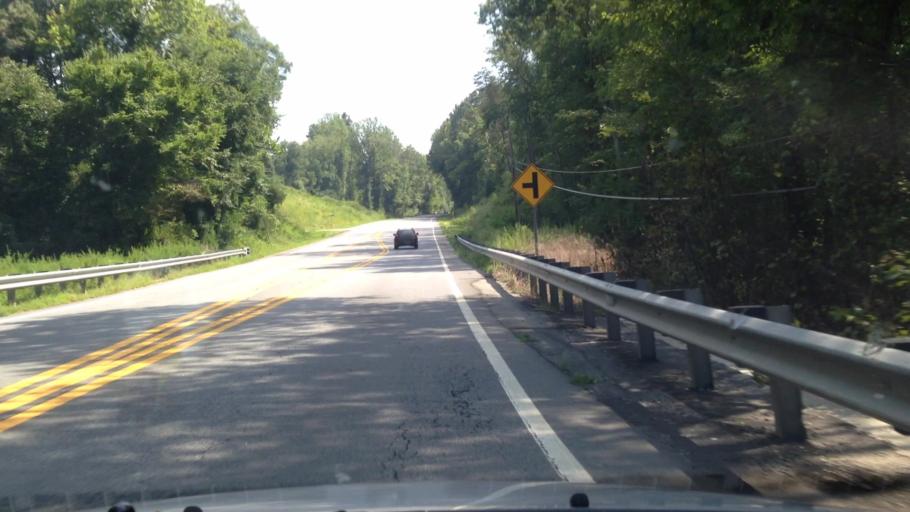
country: US
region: North Carolina
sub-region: Guilford County
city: Oak Ridge
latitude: 36.1978
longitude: -79.9853
